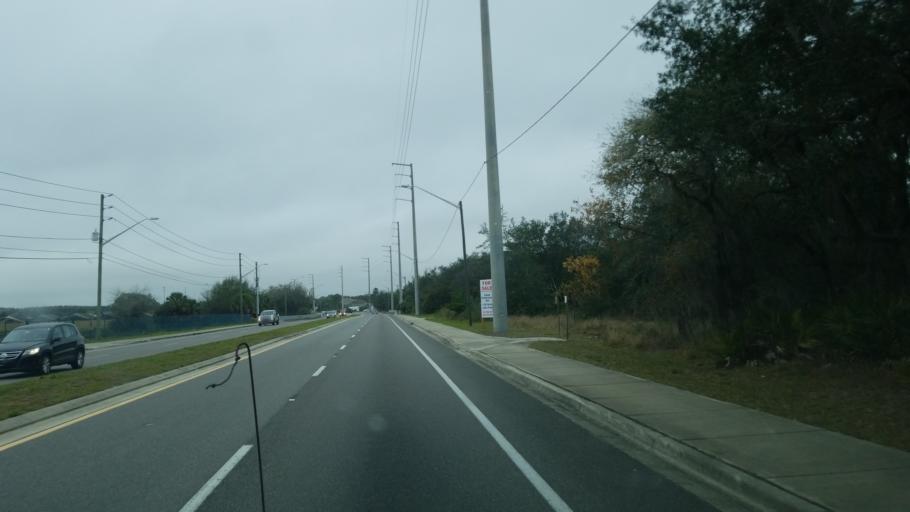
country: US
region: Florida
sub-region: Polk County
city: Loughman
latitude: 28.2577
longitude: -81.6359
